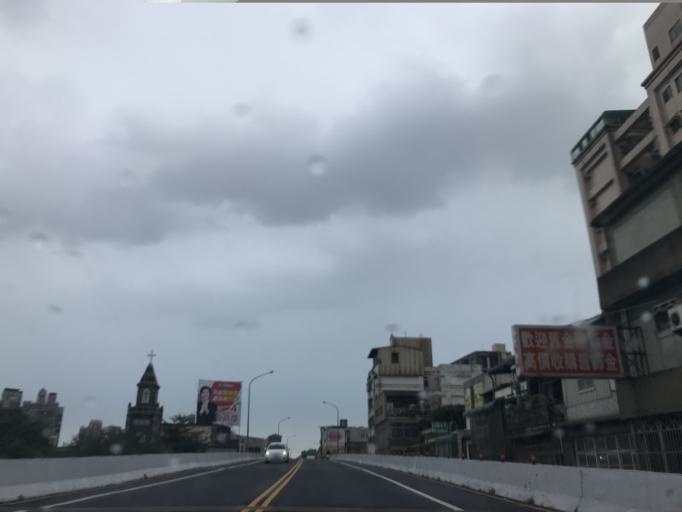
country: TW
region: Taiwan
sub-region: Hsinchu
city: Zhubei
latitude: 24.8368
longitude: 121.0092
